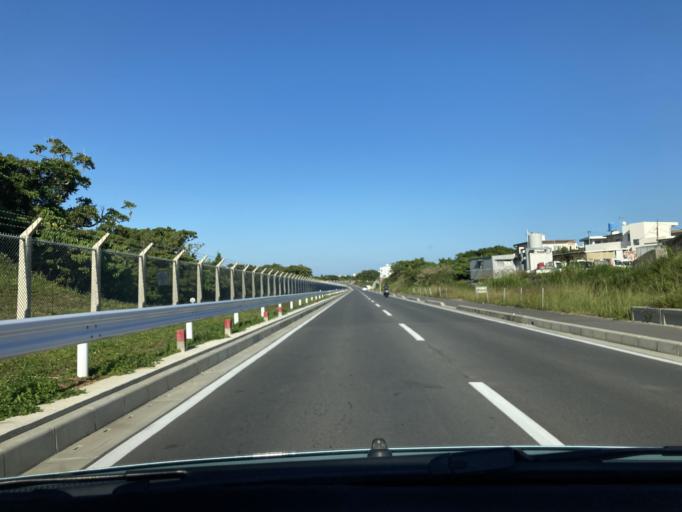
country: JP
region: Okinawa
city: Ginowan
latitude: 26.2734
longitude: 127.7680
